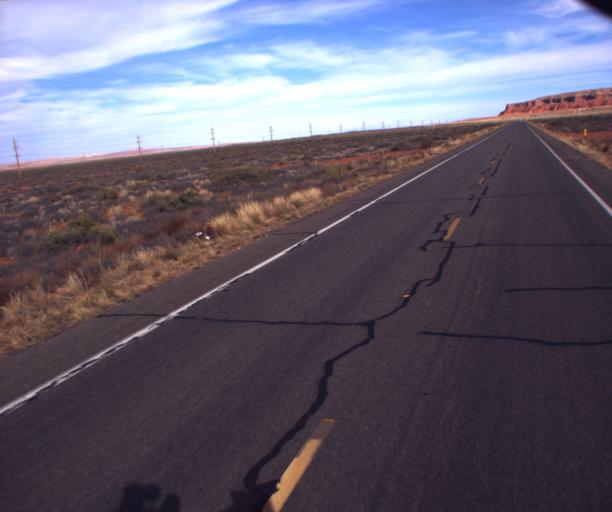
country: US
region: Arizona
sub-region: Navajo County
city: Kayenta
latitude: 36.7830
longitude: -109.9784
